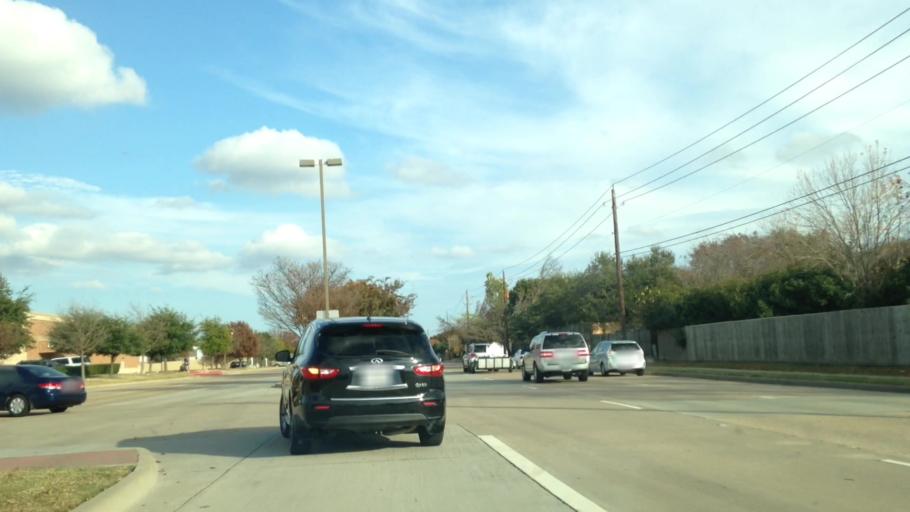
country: US
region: Texas
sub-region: Collin County
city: Allen
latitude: 33.1150
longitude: -96.6514
